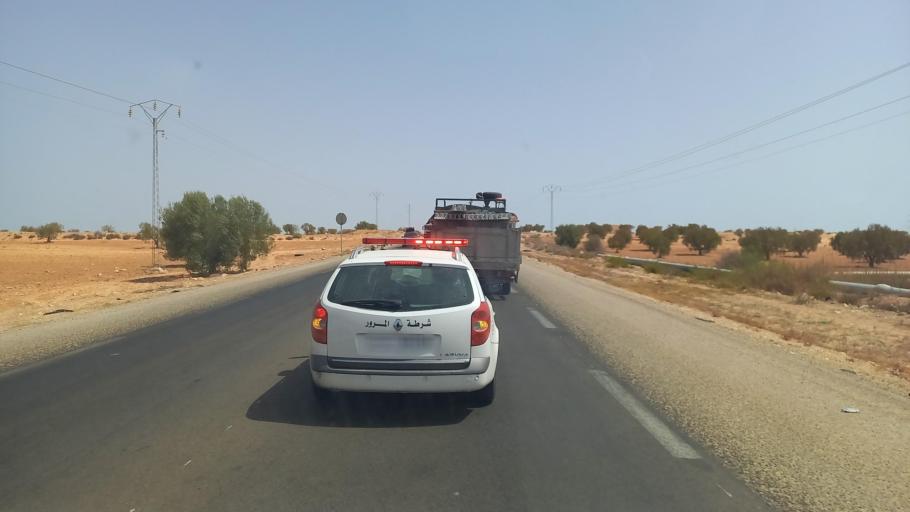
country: TN
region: Madanin
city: Zarzis
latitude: 33.4142
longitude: 10.8697
